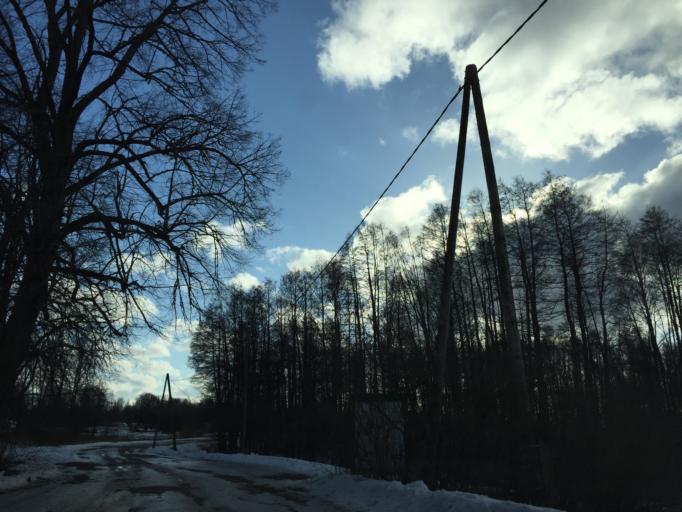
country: LV
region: Limbazu Rajons
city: Limbazi
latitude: 57.6166
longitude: 24.6107
